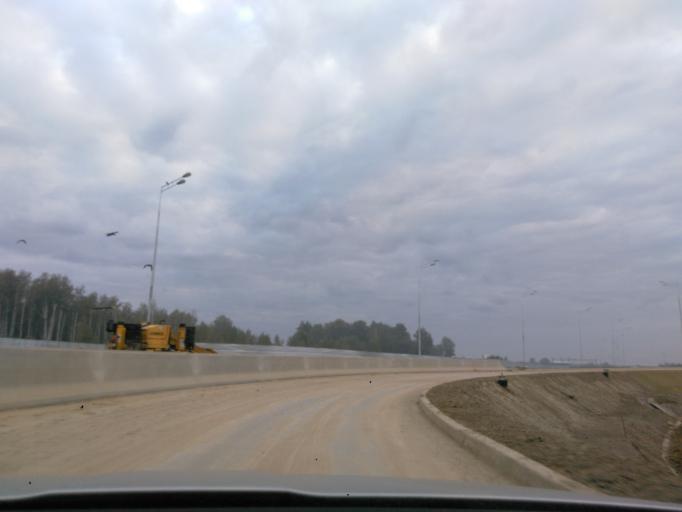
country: RU
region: Moskovskaya
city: Novopodrezkovo
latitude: 55.9643
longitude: 37.3590
